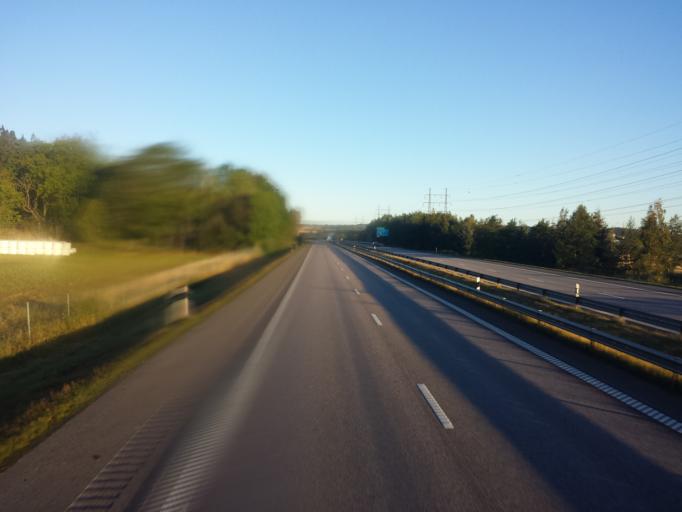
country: SE
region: Halland
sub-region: Kungsbacka Kommun
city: Kungsbacka
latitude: 57.4615
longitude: 12.0789
